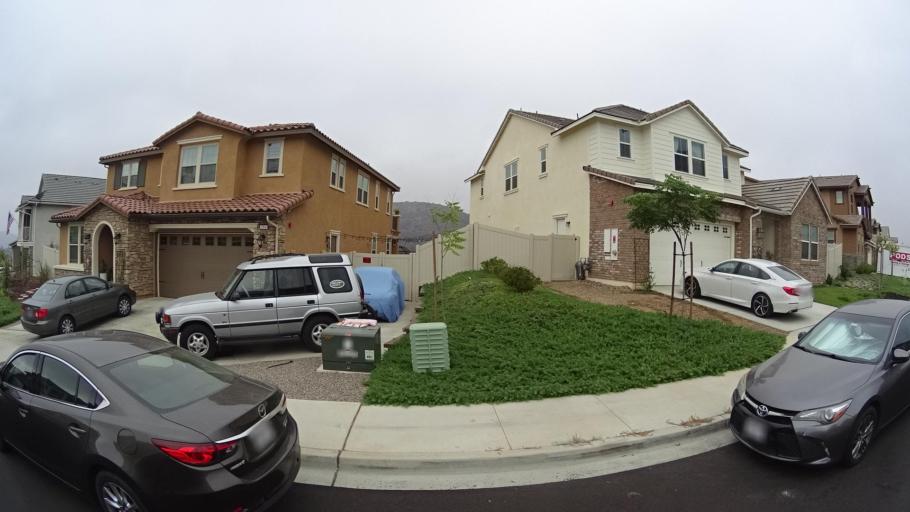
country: US
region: California
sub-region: San Diego County
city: Rainbow
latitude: 33.3595
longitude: -117.1533
